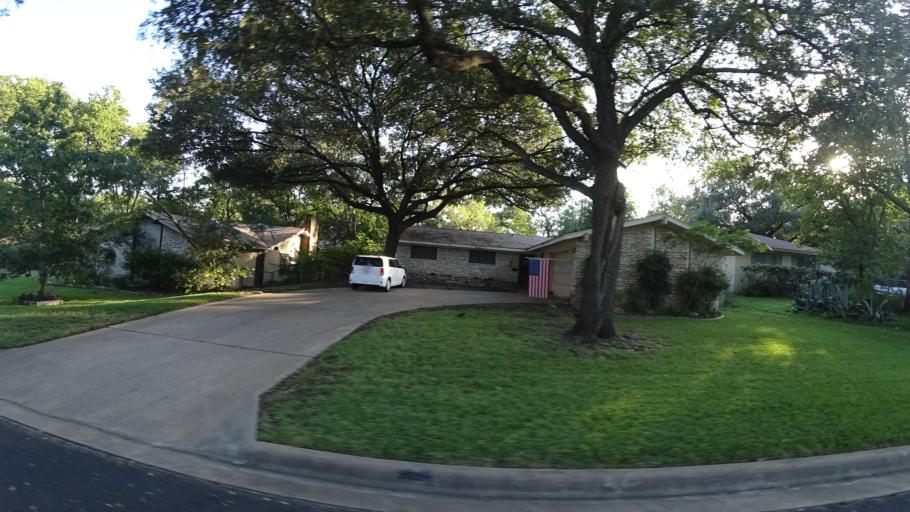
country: US
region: Texas
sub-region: Travis County
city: Wells Branch
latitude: 30.3607
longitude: -97.7025
